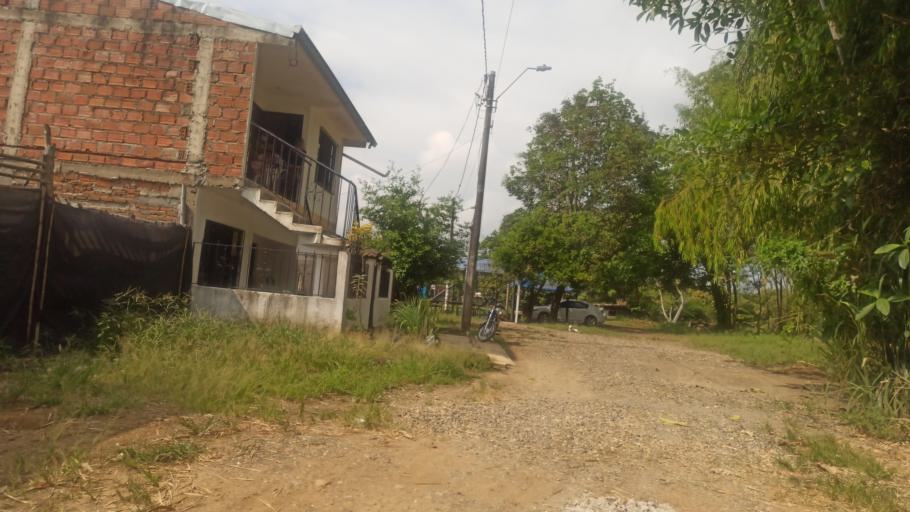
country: CO
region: Valle del Cauca
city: Jamundi
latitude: 3.1994
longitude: -76.5029
